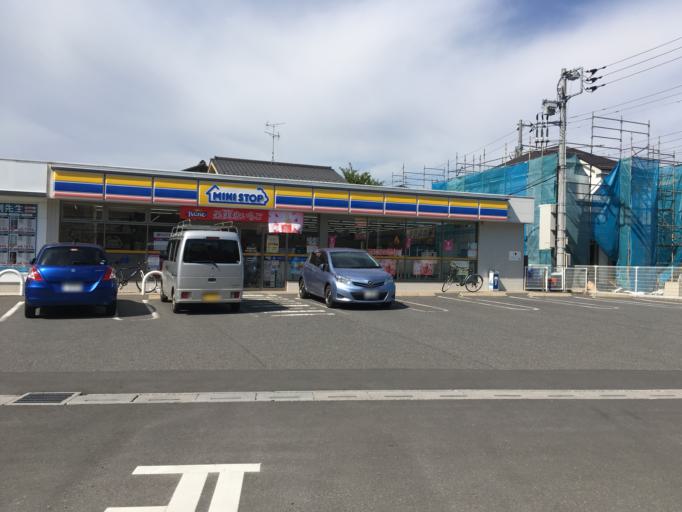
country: JP
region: Chiba
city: Kashiwa
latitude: 35.7954
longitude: 139.9794
